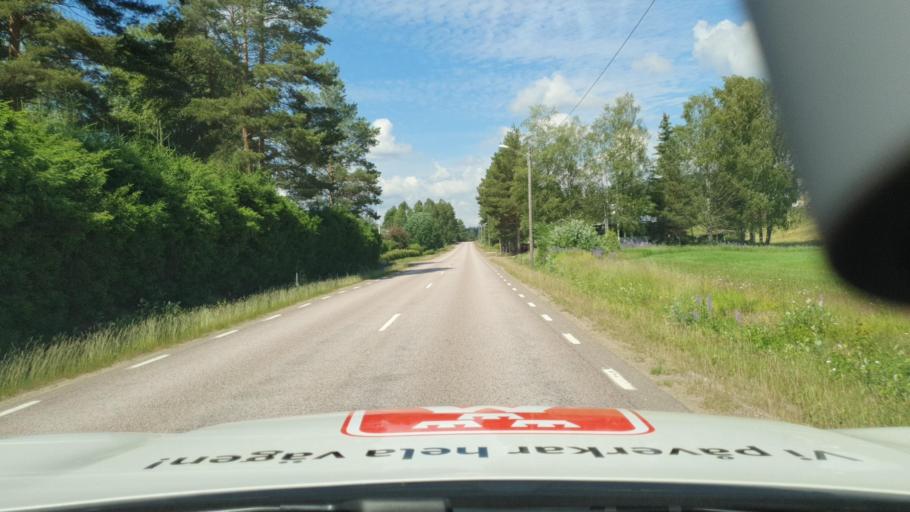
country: SE
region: Vaermland
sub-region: Torsby Kommun
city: Torsby
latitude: 60.3325
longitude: 13.0050
